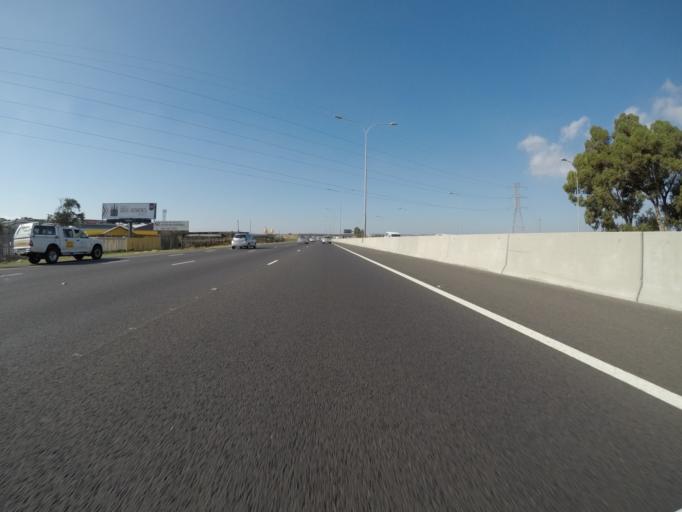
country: ZA
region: Western Cape
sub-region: City of Cape Town
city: Kraaifontein
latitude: -33.9107
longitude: 18.6706
